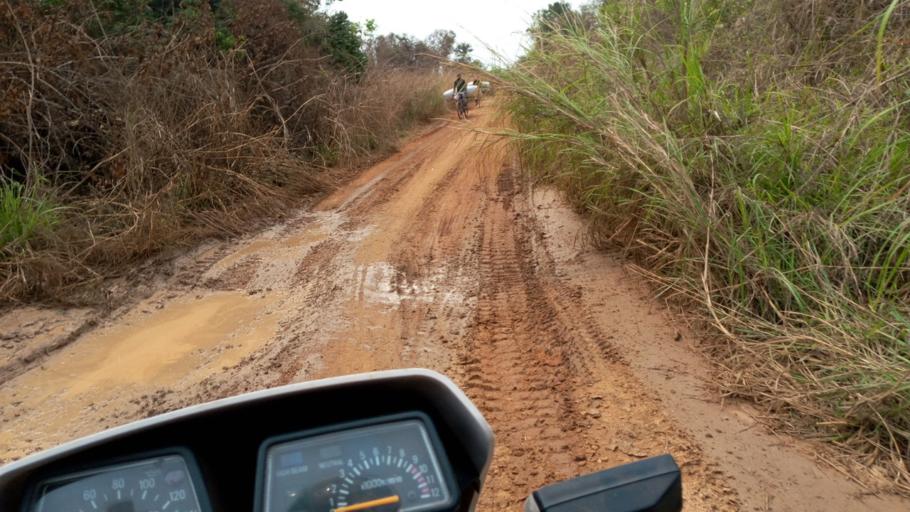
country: CD
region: Bandundu
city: Bandundu
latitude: -3.4688
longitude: 17.7766
